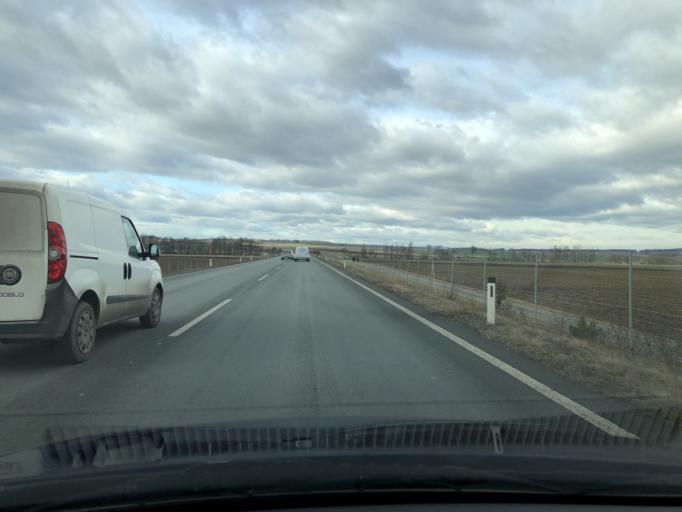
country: AT
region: Burgenland
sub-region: Politischer Bezirk Oberwart
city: Markt Neuhodis
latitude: 47.2761
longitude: 16.4100
